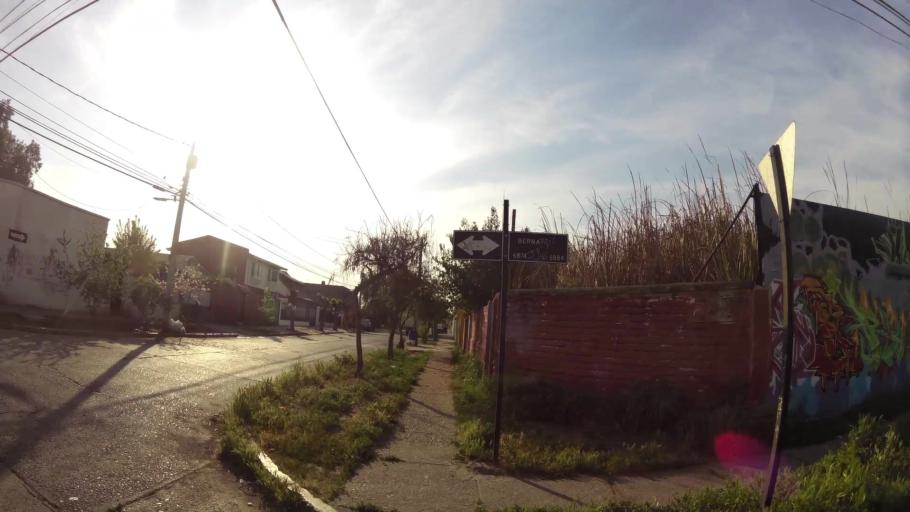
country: CL
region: Santiago Metropolitan
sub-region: Provincia de Santiago
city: Santiago
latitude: -33.5180
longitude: -70.6699
